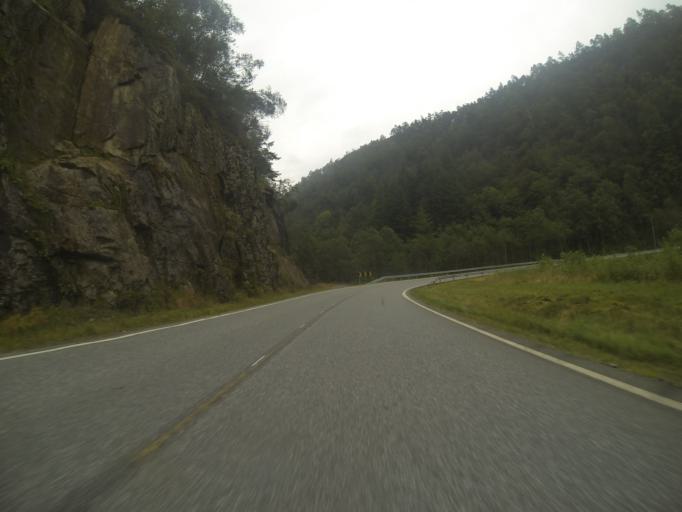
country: NO
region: Rogaland
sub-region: Suldal
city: Sand
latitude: 59.5383
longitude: 6.2532
